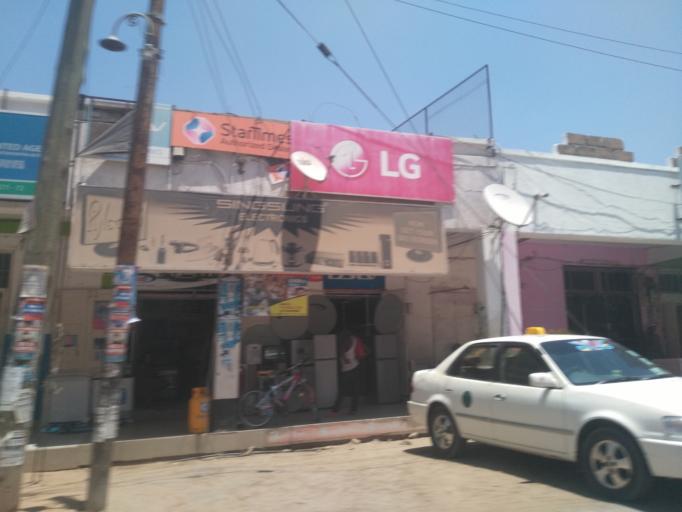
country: TZ
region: Dodoma
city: Dodoma
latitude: -6.1805
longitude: 35.7484
